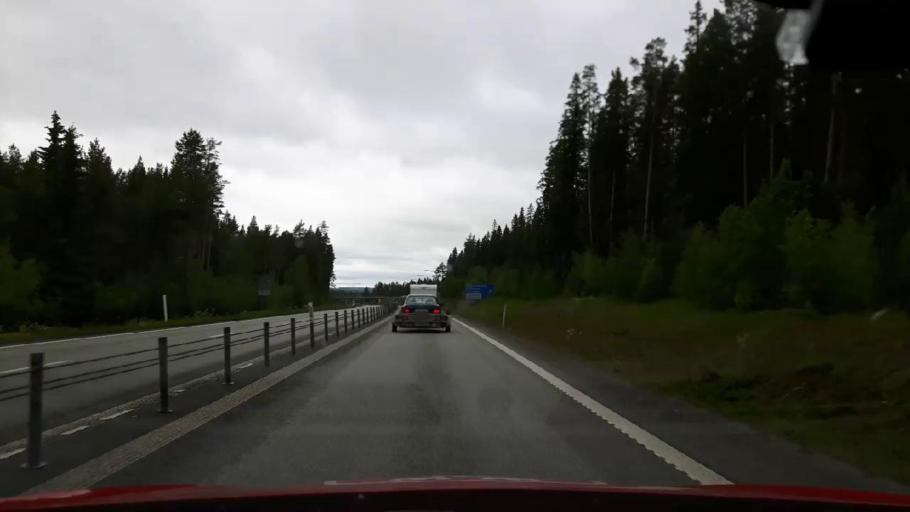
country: SE
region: Jaemtland
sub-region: OEstersunds Kommun
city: Ostersund
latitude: 63.2003
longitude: 14.6821
